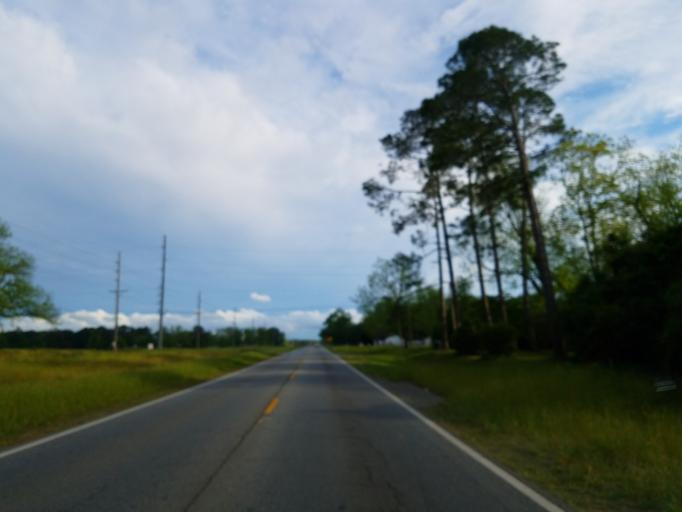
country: US
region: Georgia
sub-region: Crisp County
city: Cordele
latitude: 31.9970
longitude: -83.7945
